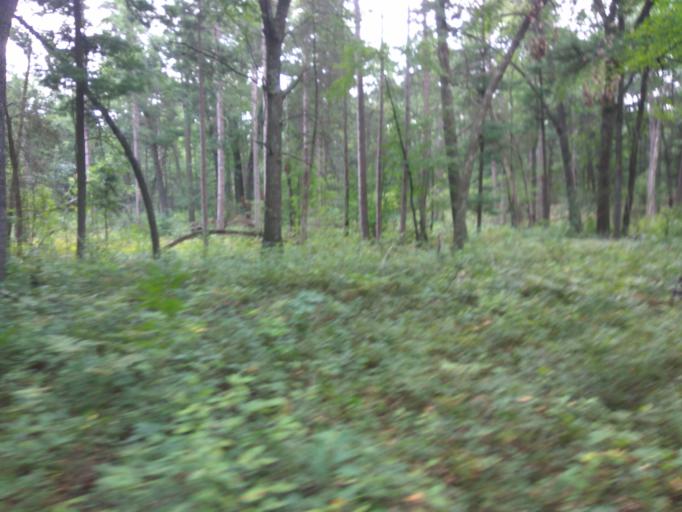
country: CA
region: Ontario
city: Lambton Shores
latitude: 43.2481
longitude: -81.8561
